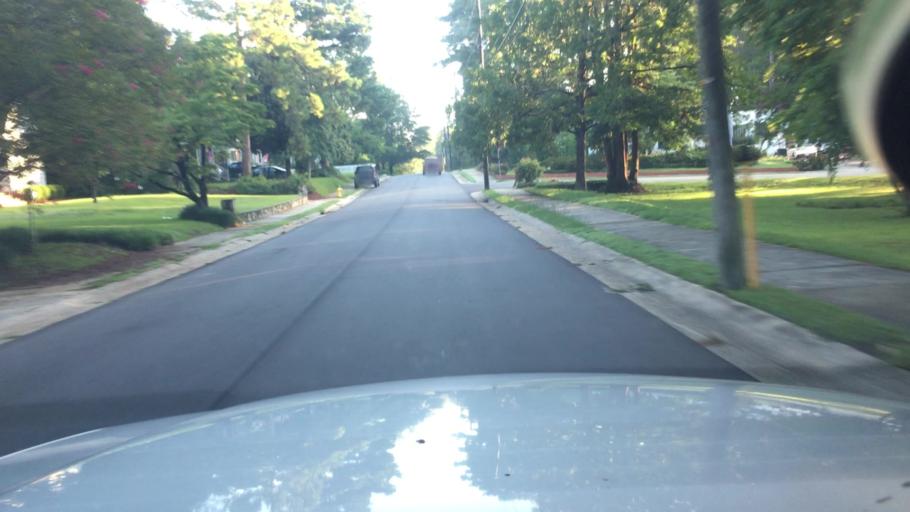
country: US
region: North Carolina
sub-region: Cumberland County
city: Fayetteville
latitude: 35.0631
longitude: -78.9074
